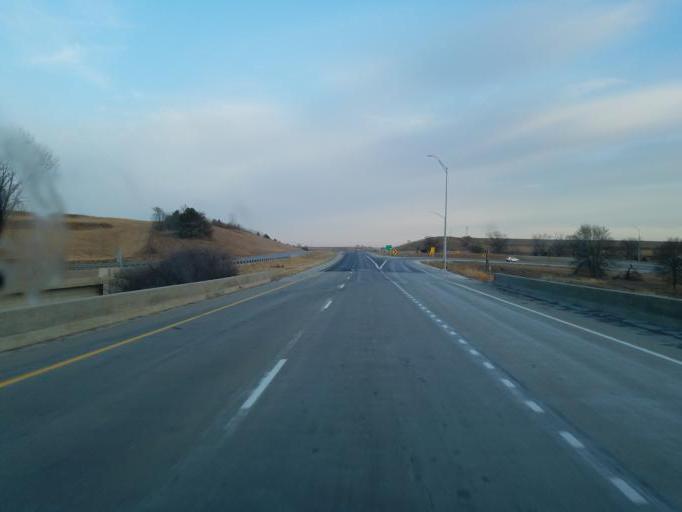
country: US
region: Iowa
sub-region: Harrison County
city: Logan
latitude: 41.4986
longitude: -95.7462
